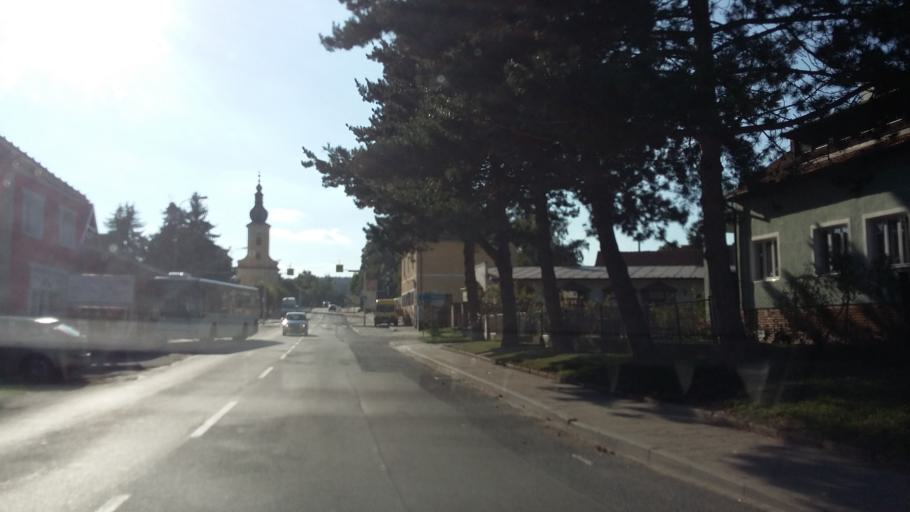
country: CZ
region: South Moravian
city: Ricany
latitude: 49.2147
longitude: 16.3960
